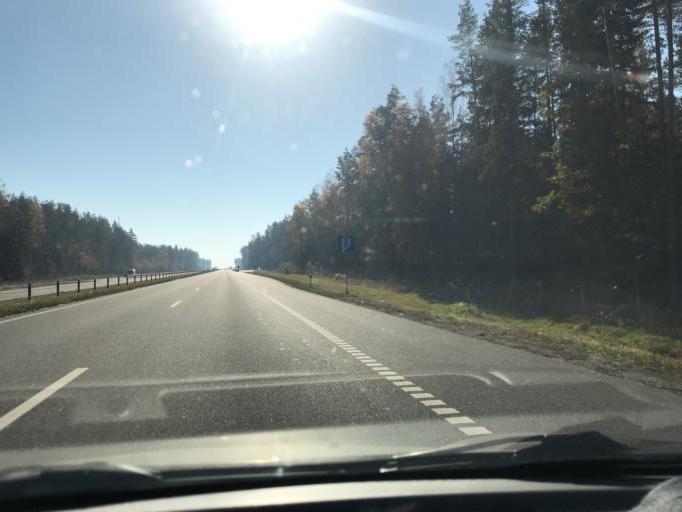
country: BY
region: Mogilev
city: Babruysk
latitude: 53.2052
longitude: 29.3471
